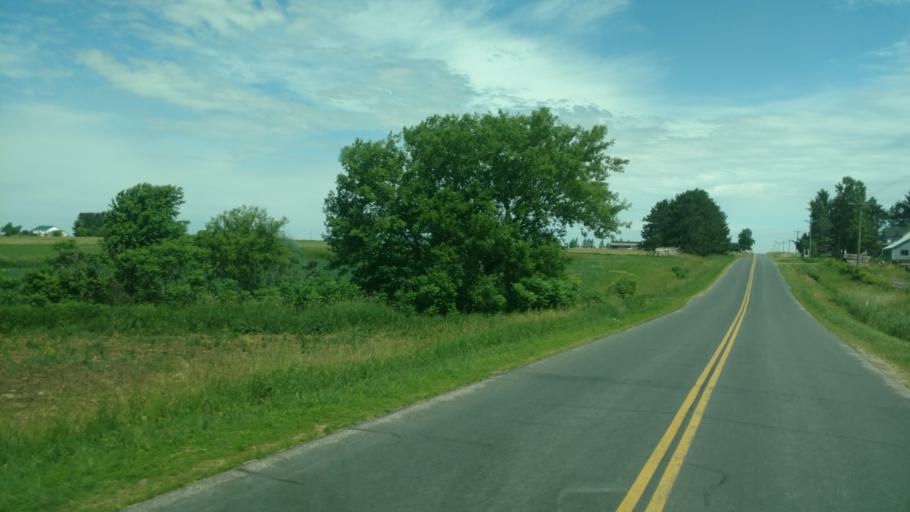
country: US
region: Wisconsin
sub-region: Vernon County
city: Hillsboro
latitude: 43.7552
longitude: -90.4330
